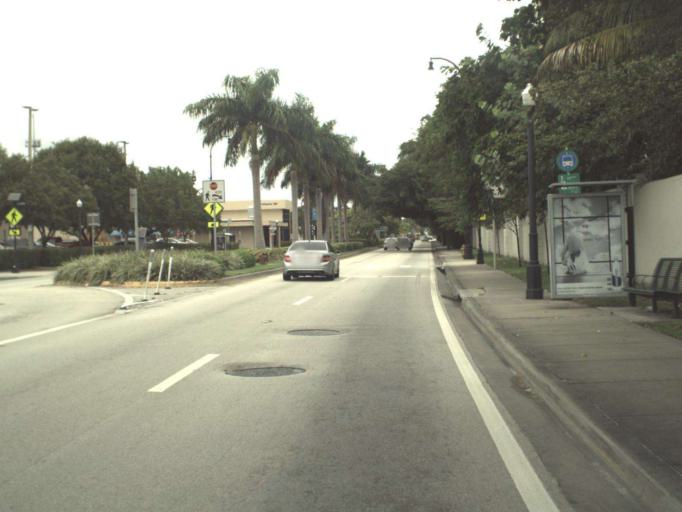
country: US
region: Florida
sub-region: Miami-Dade County
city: El Portal
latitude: 25.8194
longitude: -80.1877
